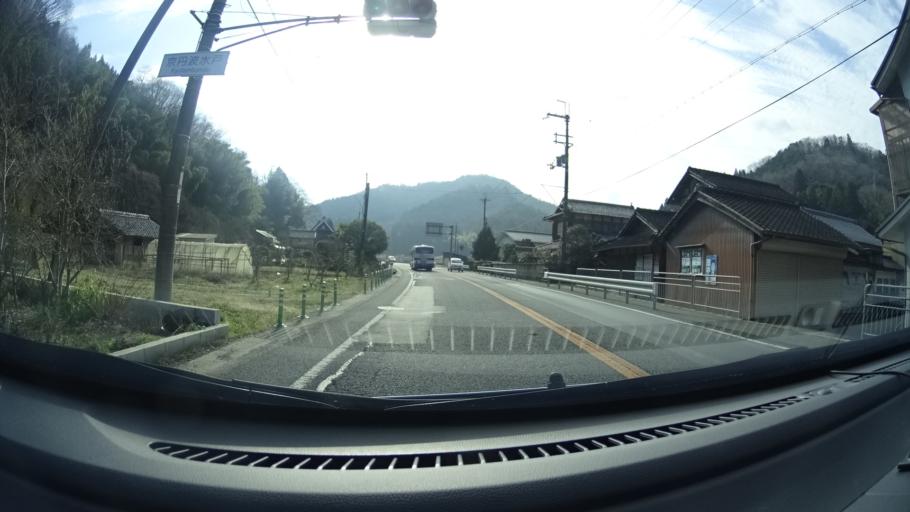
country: JP
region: Kyoto
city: Kameoka
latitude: 35.1396
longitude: 135.4255
